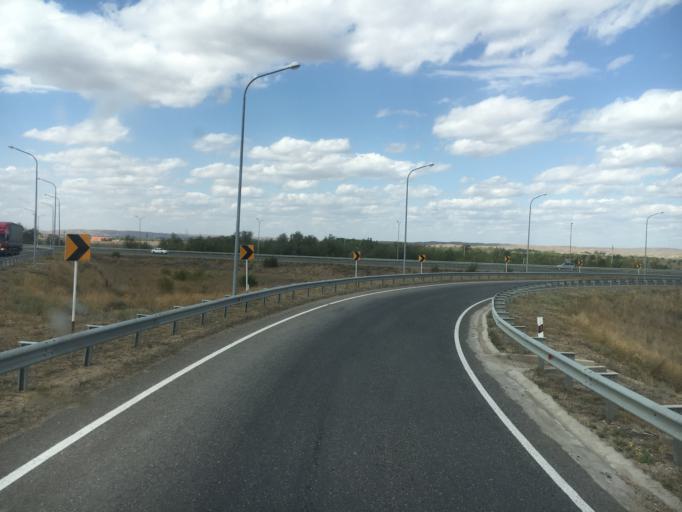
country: KZ
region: Aqtoebe
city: Aqtobe
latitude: 50.2927
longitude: 57.4346
